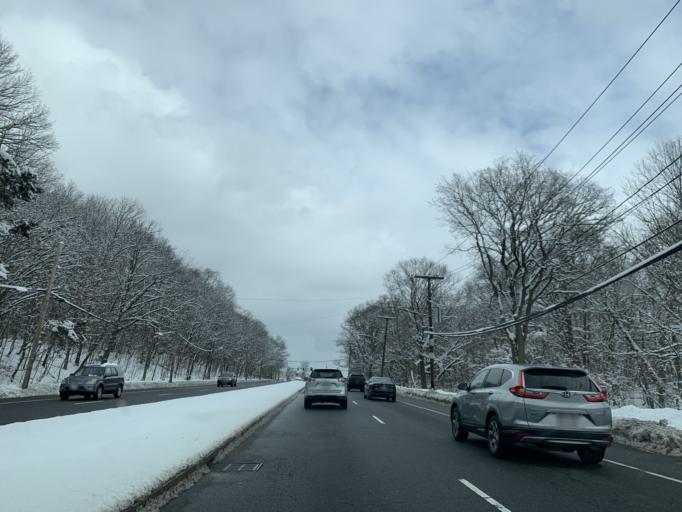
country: US
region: Massachusetts
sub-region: Norfolk County
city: Dedham
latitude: 42.2735
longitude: -71.1428
